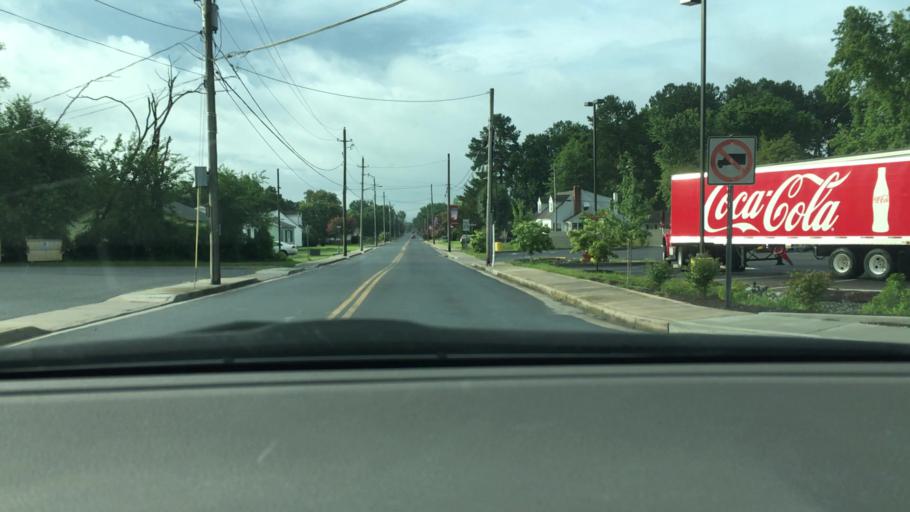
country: US
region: Maryland
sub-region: Wicomico County
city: Fruitland
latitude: 38.3277
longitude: -75.6235
